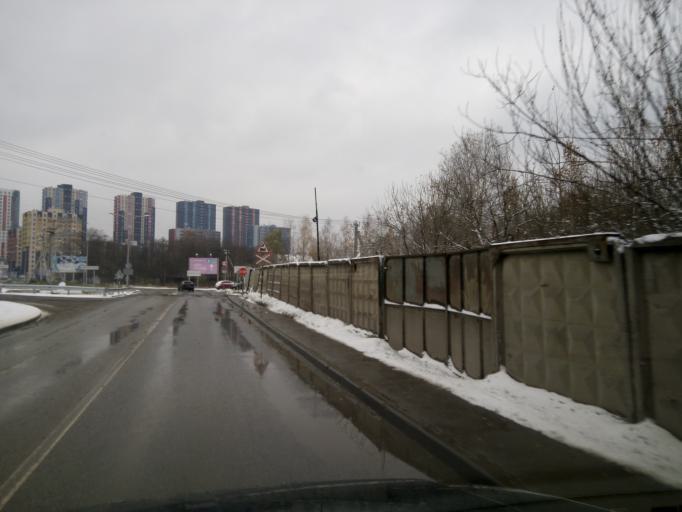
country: RU
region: Moskovskaya
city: Skhodnya
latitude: 55.9412
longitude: 37.2696
